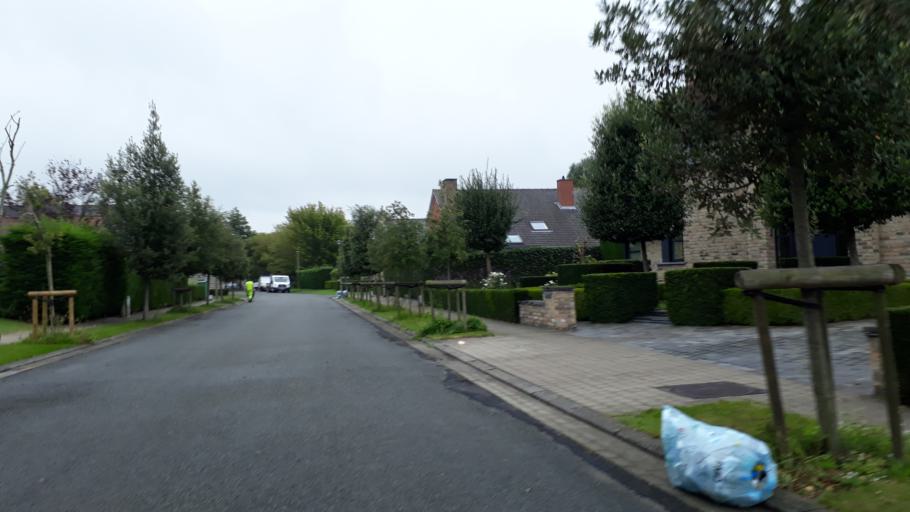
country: BE
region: Flanders
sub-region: Provincie West-Vlaanderen
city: Torhout
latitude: 51.0664
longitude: 3.1107
